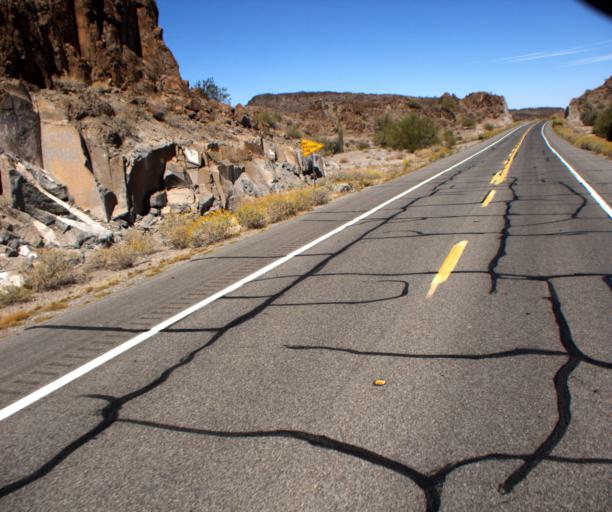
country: US
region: Arizona
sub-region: Pima County
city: Ajo
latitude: 32.5476
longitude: -112.8800
